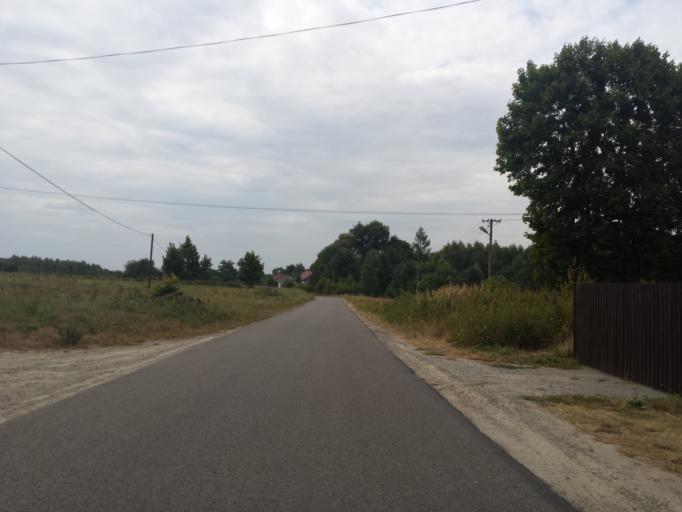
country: PL
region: Swietokrzyskie
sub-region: Powiat staszowski
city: Bogoria
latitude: 50.6574
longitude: 21.2127
